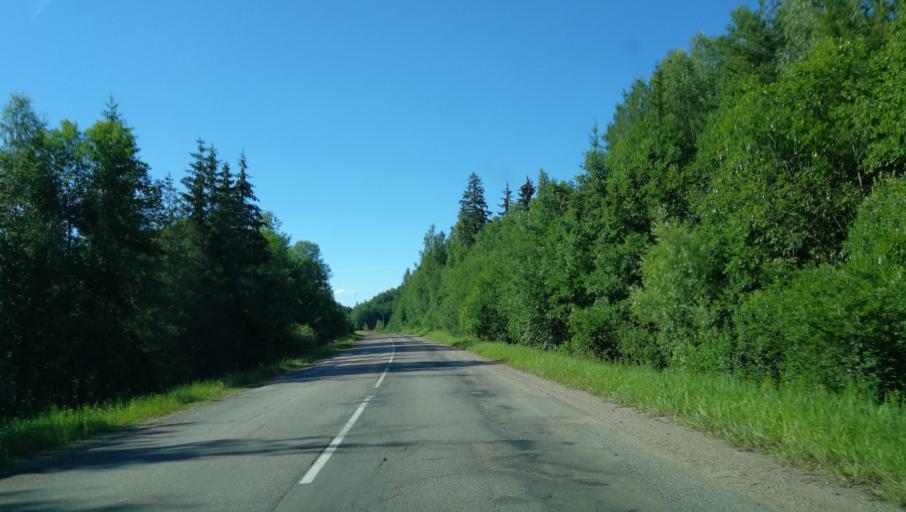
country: LV
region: Jaunpiebalga
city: Jaunpiebalga
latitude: 56.9744
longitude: 26.0443
